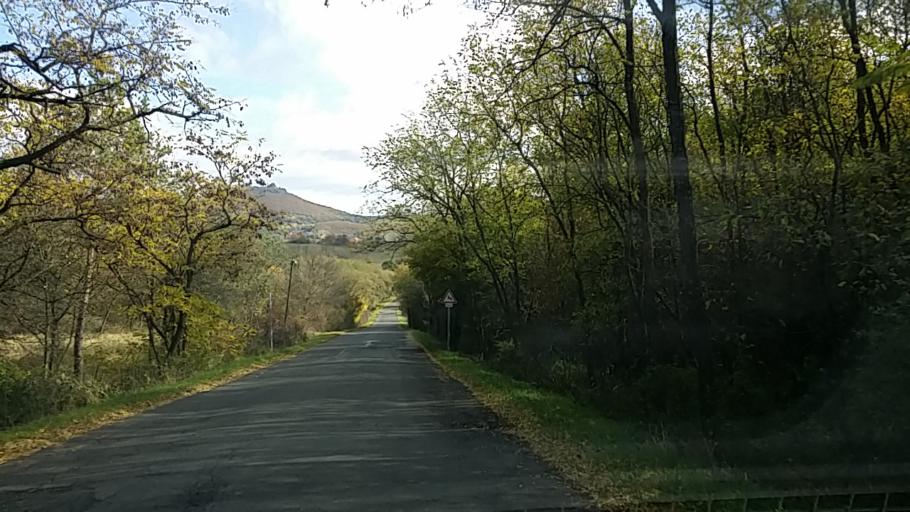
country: HU
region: Borsod-Abauj-Zemplen
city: Gonc
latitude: 48.3852
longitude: 21.3053
